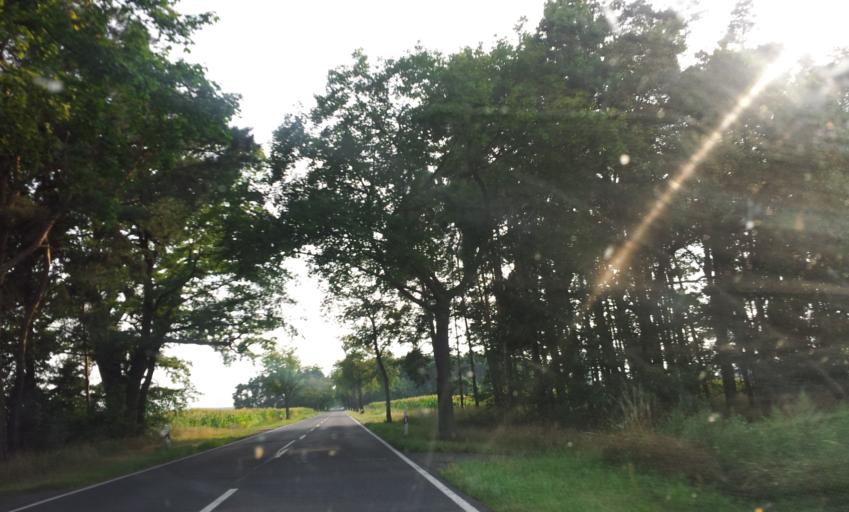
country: DE
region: Brandenburg
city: Treuenbrietzen
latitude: 52.1170
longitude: 12.9732
